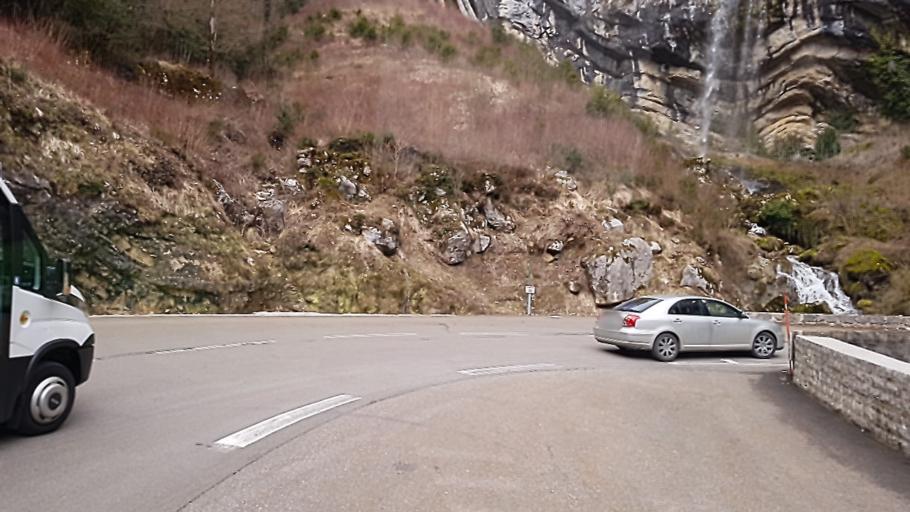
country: FR
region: Franche-Comte
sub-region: Departement du Jura
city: Saint-Claude
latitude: 46.3586
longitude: 5.9051
